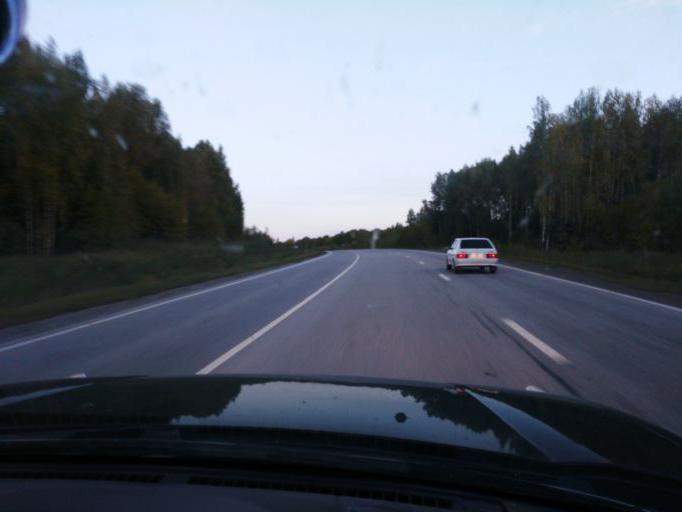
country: RU
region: Perm
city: Verkhnechusovskiye Gorodki
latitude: 58.2862
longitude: 56.8976
